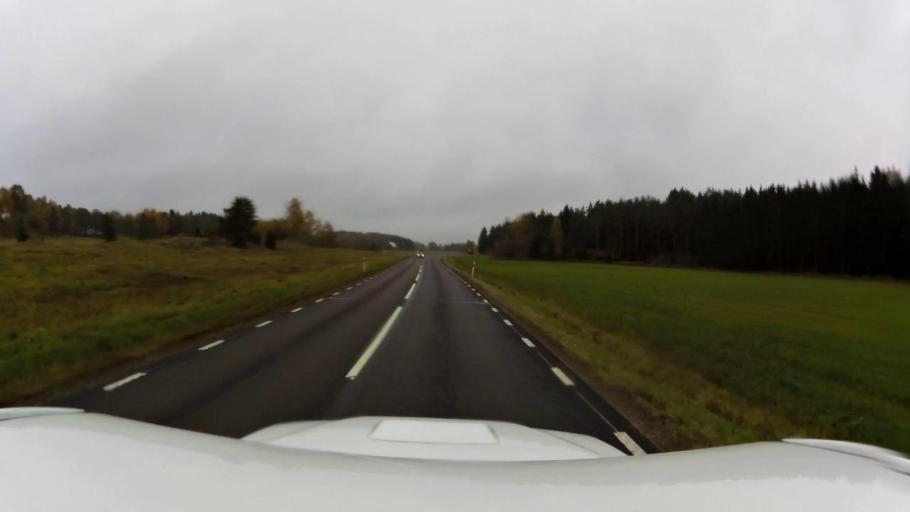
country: SE
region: OEstergoetland
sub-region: Linkopings Kommun
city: Linghem
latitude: 58.3655
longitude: 15.8218
